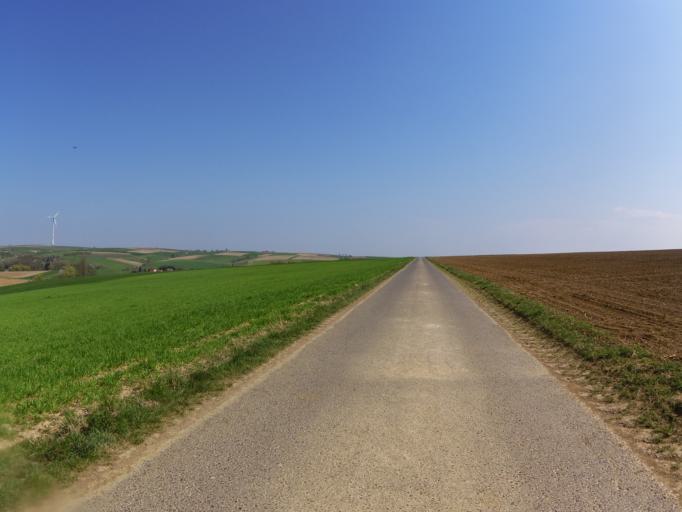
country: DE
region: Bavaria
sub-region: Regierungsbezirk Unterfranken
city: Dettelbach
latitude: 49.8158
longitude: 10.1396
